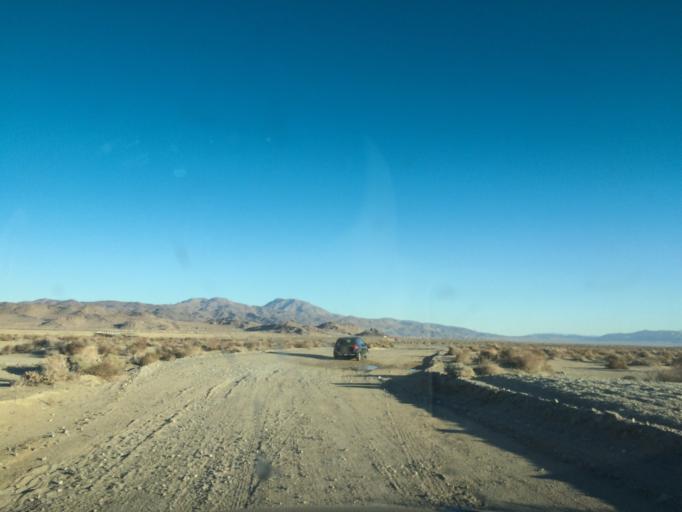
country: US
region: California
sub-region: San Bernardino County
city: Searles Valley
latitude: 35.6610
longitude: -117.3784
